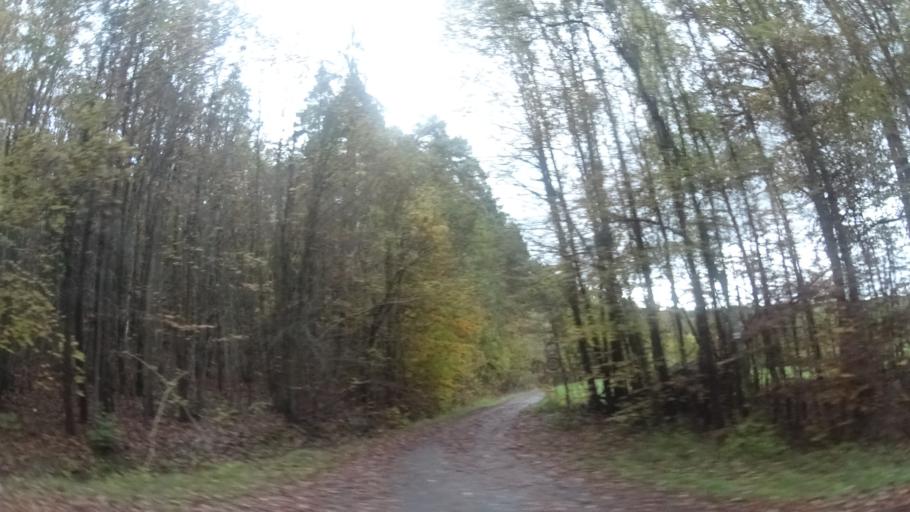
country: DE
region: Bavaria
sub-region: Regierungsbezirk Unterfranken
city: Oberelsbach
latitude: 50.3596
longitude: 10.0994
